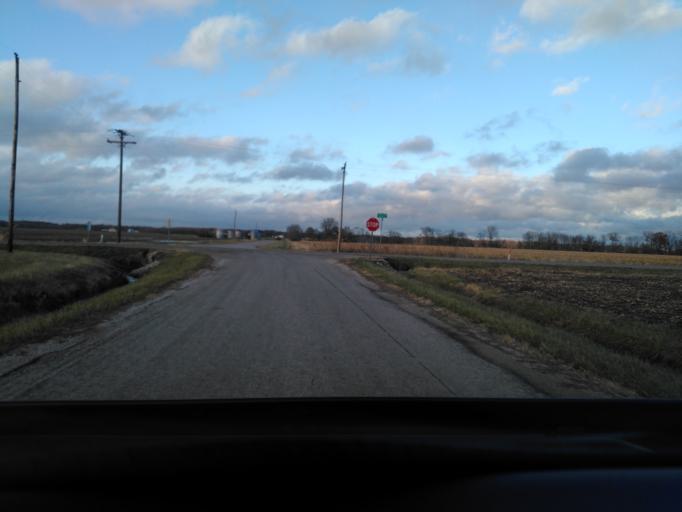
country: US
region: Illinois
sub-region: Effingham County
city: Altamont
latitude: 38.9577
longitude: -88.7116
